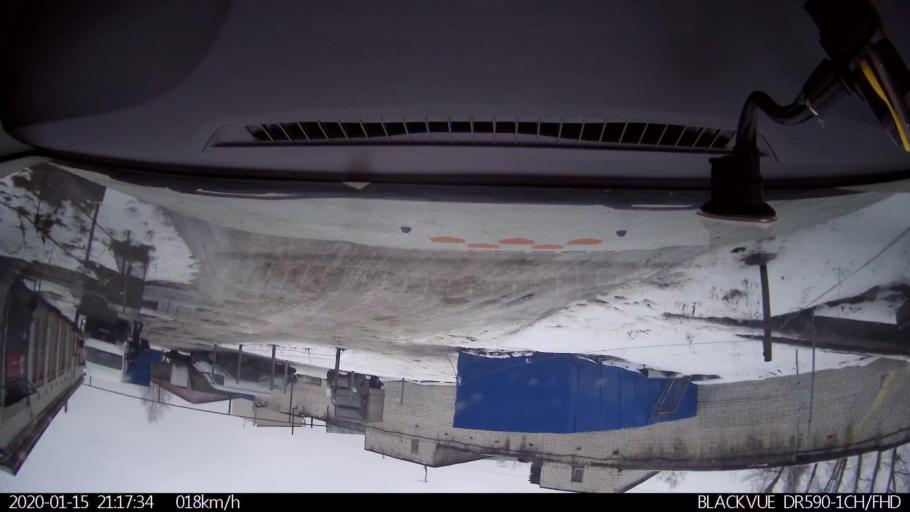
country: RU
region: Nizjnij Novgorod
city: Gorbatovka
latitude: 56.3000
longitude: 43.8600
